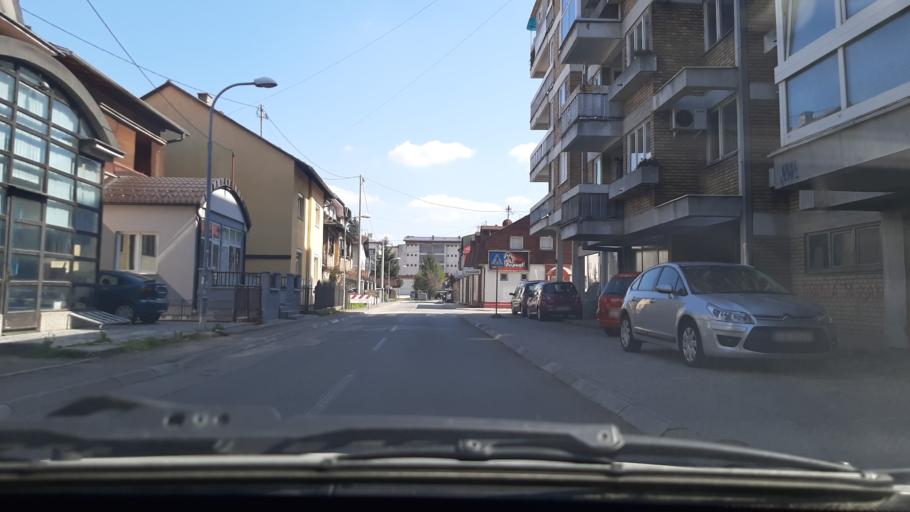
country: BA
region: Republika Srpska
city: Hiseti
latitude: 44.7675
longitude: 17.1832
